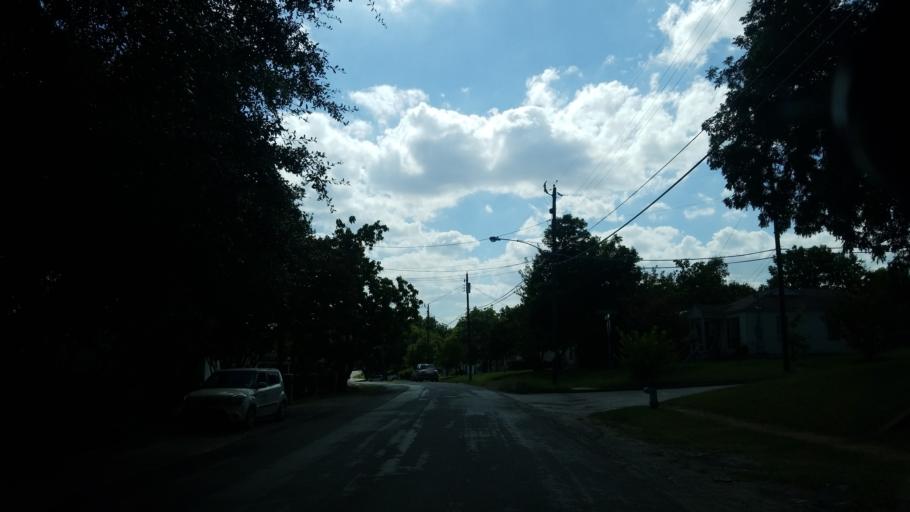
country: US
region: Texas
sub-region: Dallas County
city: Balch Springs
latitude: 32.7715
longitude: -96.7071
